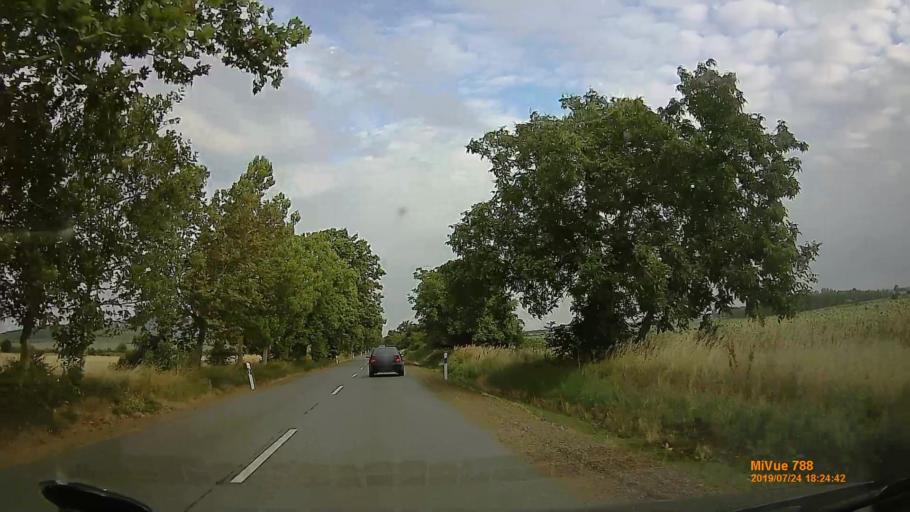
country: HU
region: Borsod-Abauj-Zemplen
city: Mezozombor
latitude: 48.1602
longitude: 21.3086
